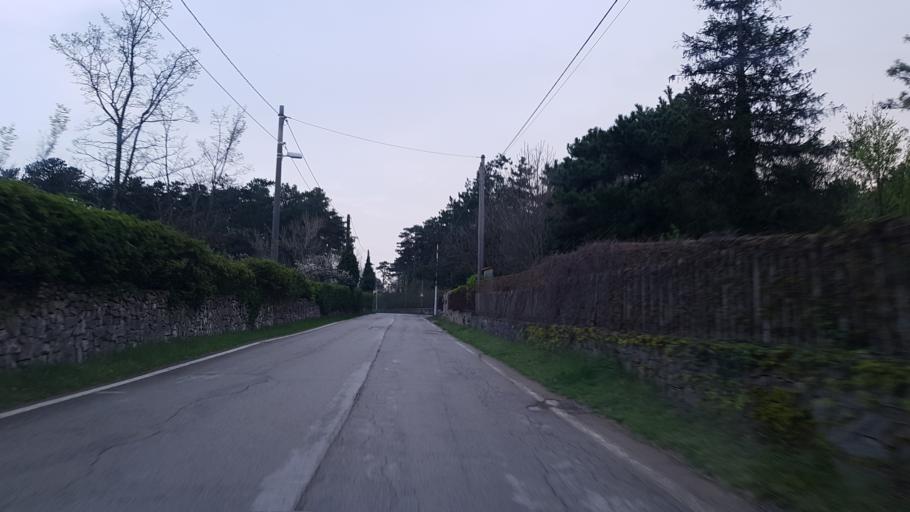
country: IT
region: Friuli Venezia Giulia
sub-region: Provincia di Trieste
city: Domio
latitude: 45.6499
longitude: 13.8393
